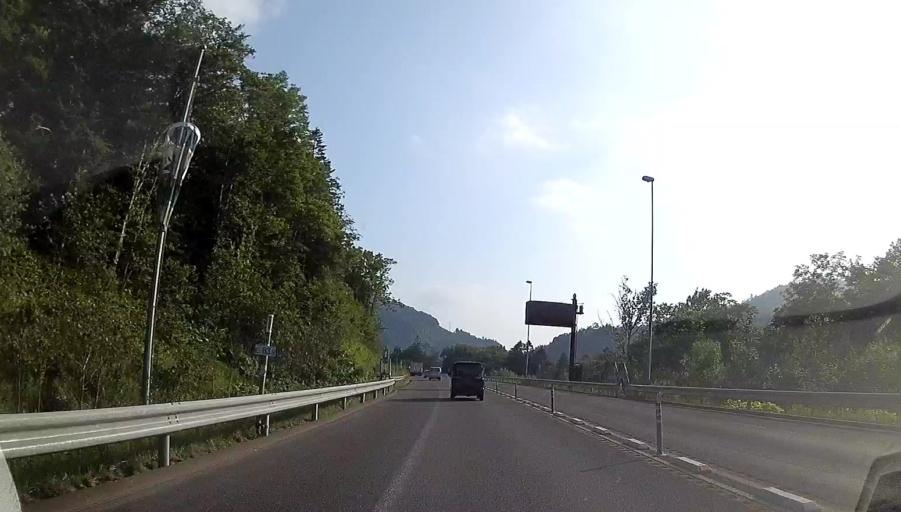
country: JP
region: Hokkaido
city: Shimo-furano
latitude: 43.0295
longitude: 142.4553
